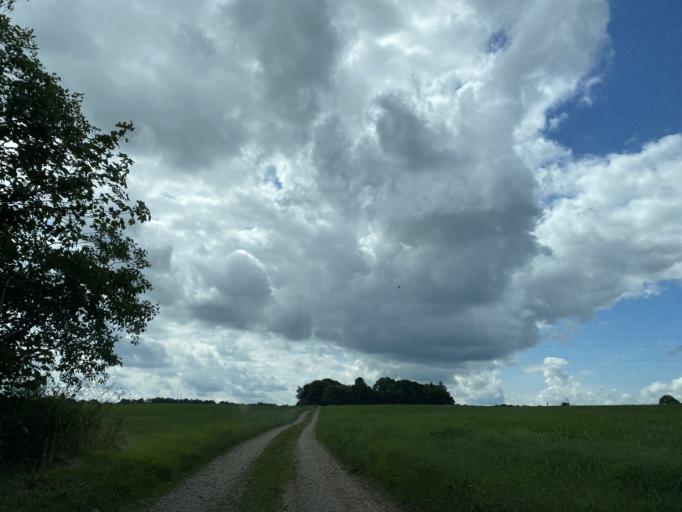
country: DK
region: Central Jutland
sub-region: Silkeborg Kommune
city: Silkeborg
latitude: 56.2136
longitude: 9.5753
